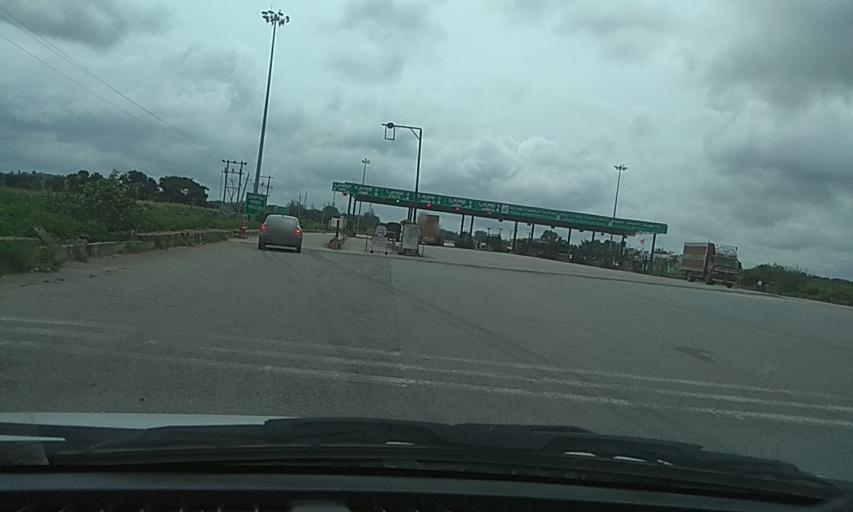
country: IN
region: Karnataka
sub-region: Davanagere
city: Mayakonda
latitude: 14.3761
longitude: 76.1057
